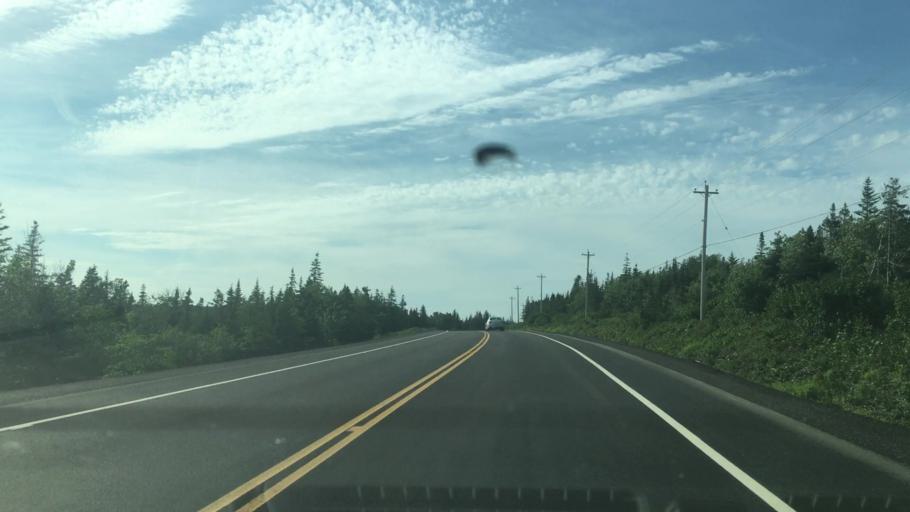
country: CA
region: Nova Scotia
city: Sydney Mines
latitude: 46.8439
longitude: -60.4042
